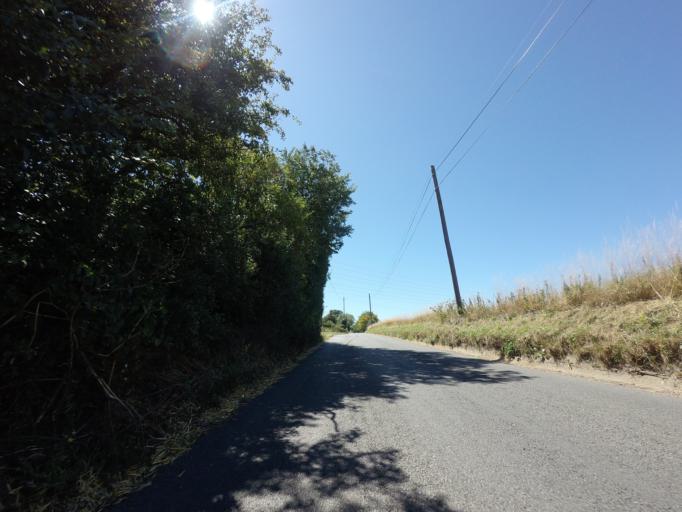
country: GB
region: England
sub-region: Kent
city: Eastry
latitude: 51.2545
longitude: 1.3075
